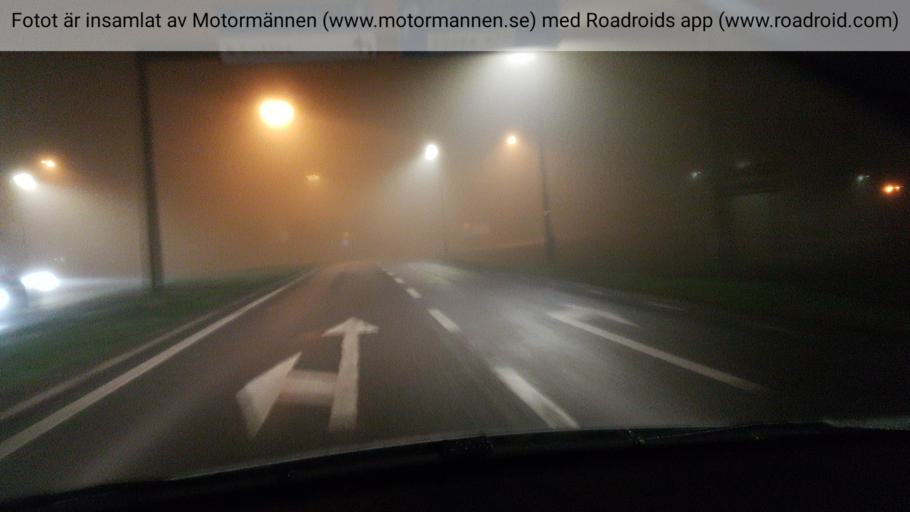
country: SE
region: Vaestra Goetaland
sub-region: Skovde Kommun
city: Skoevde
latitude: 58.4184
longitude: 13.8686
